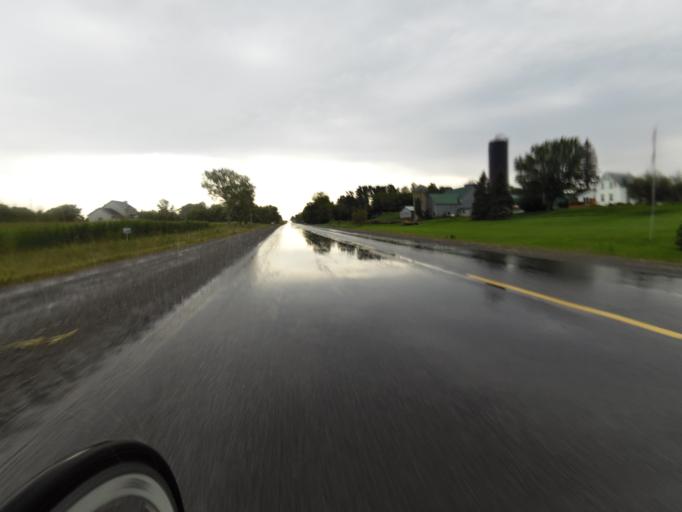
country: CA
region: Ontario
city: Bells Corners
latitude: 45.1779
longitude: -75.7184
